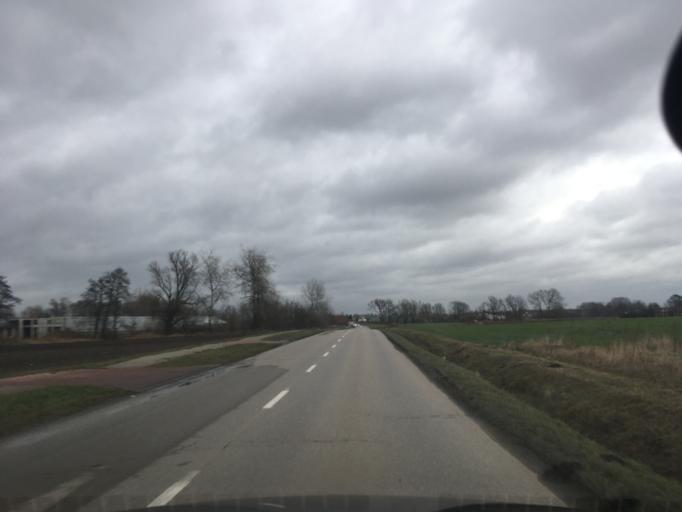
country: PL
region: Masovian Voivodeship
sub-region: Powiat pruszkowski
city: Rybie
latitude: 52.1297
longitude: 20.9660
